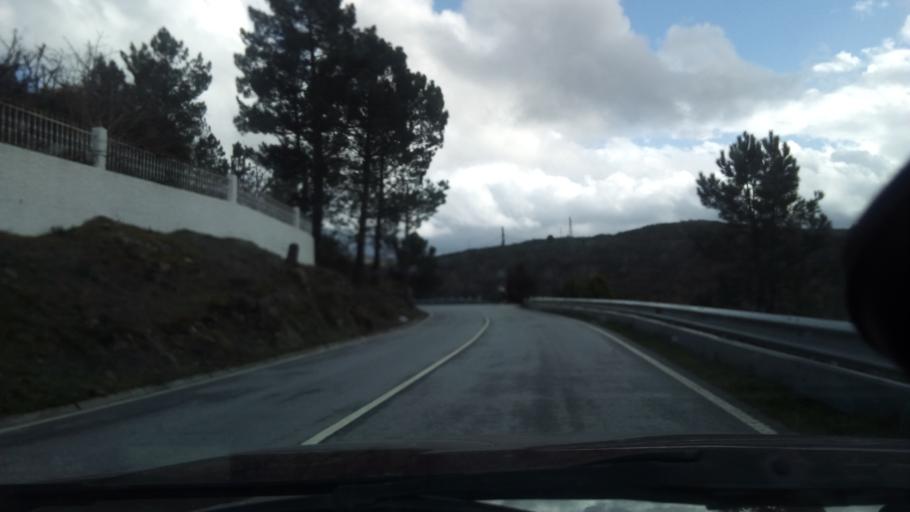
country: PT
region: Guarda
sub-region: Guarda
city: Guarda
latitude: 40.5405
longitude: -7.3150
